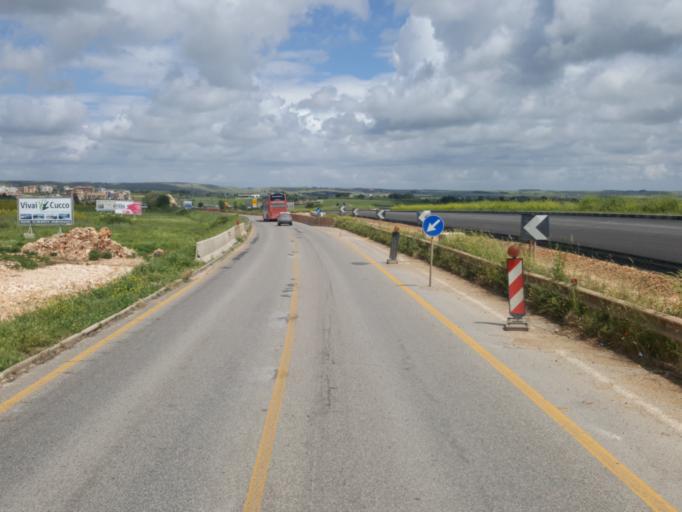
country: IT
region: Apulia
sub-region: Provincia di Bari
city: Altamura
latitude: 40.8187
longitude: 16.5692
